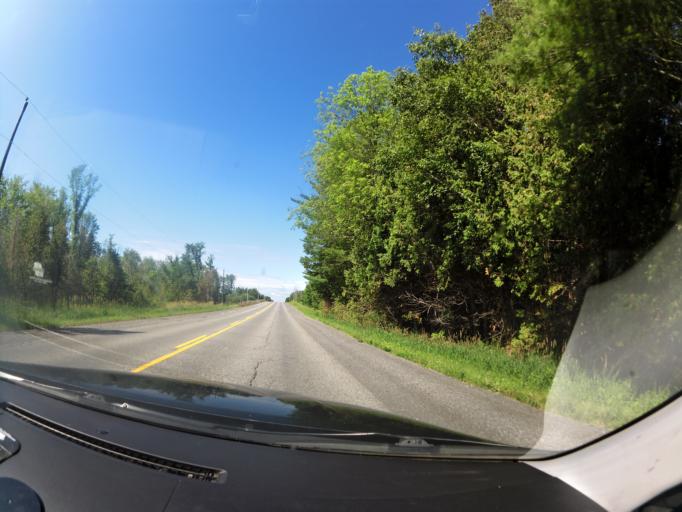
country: CA
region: Ontario
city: Carleton Place
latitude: 45.1465
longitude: -76.3169
